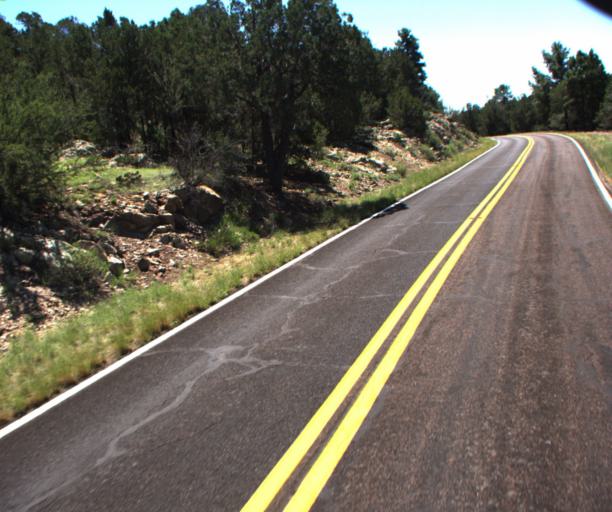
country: US
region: Arizona
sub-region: Greenlee County
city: Morenci
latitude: 33.3836
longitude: -109.3316
